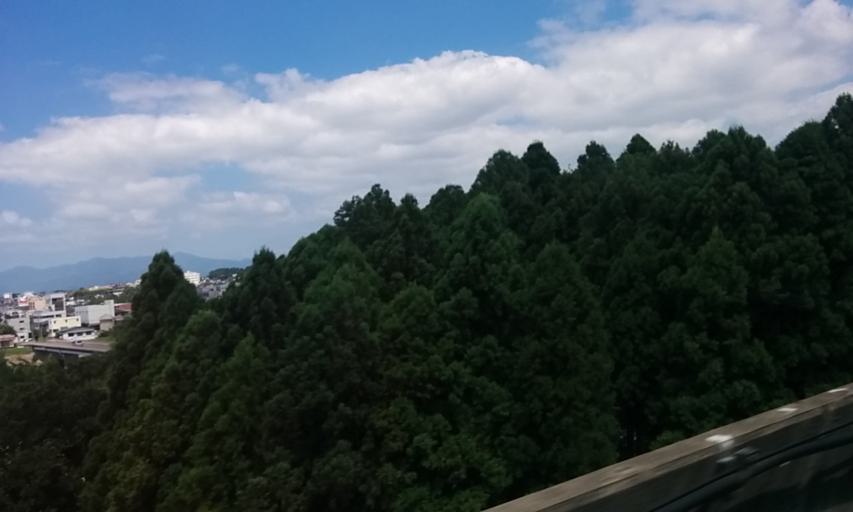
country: JP
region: Fukushima
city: Koriyama
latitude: 37.3554
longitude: 140.3736
